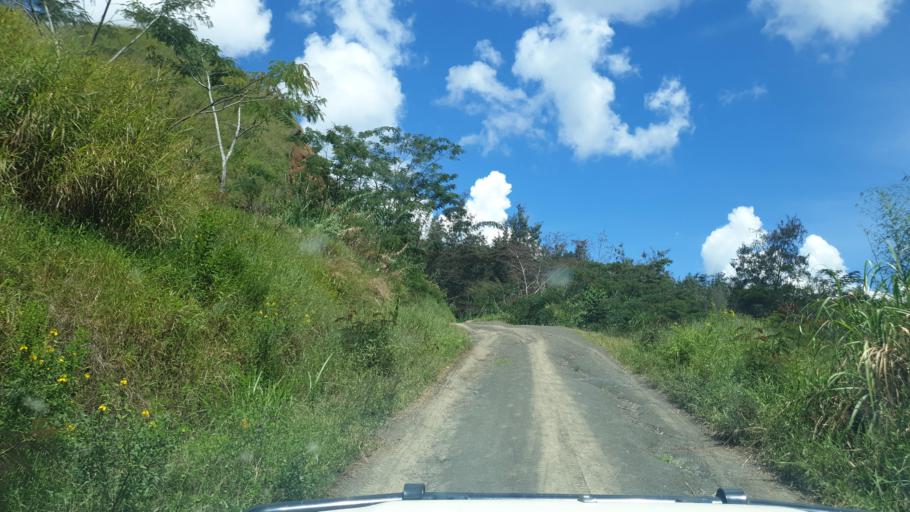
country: PG
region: Chimbu
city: Kundiawa
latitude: -6.2569
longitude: 145.1380
